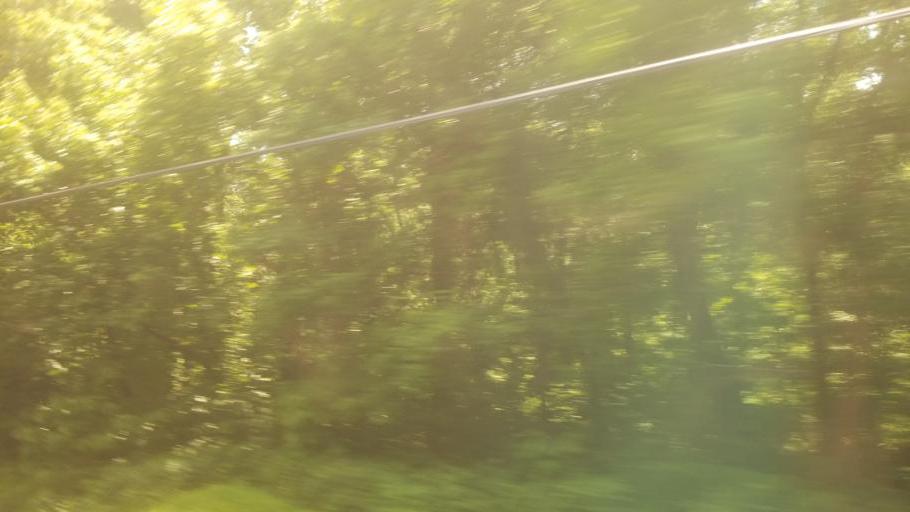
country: US
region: Maryland
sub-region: Frederick County
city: Point of Rocks
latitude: 39.2849
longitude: -77.5499
